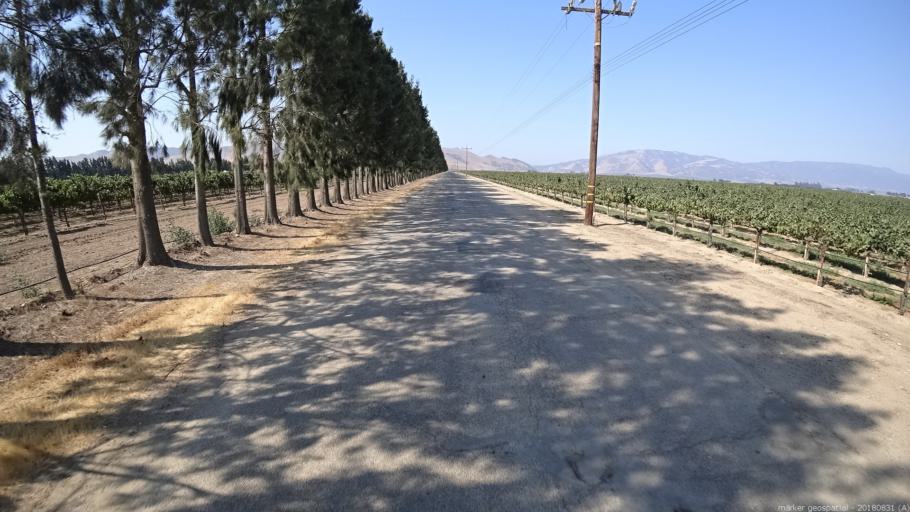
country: US
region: California
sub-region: Monterey County
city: Greenfield
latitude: 36.3050
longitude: -121.2362
